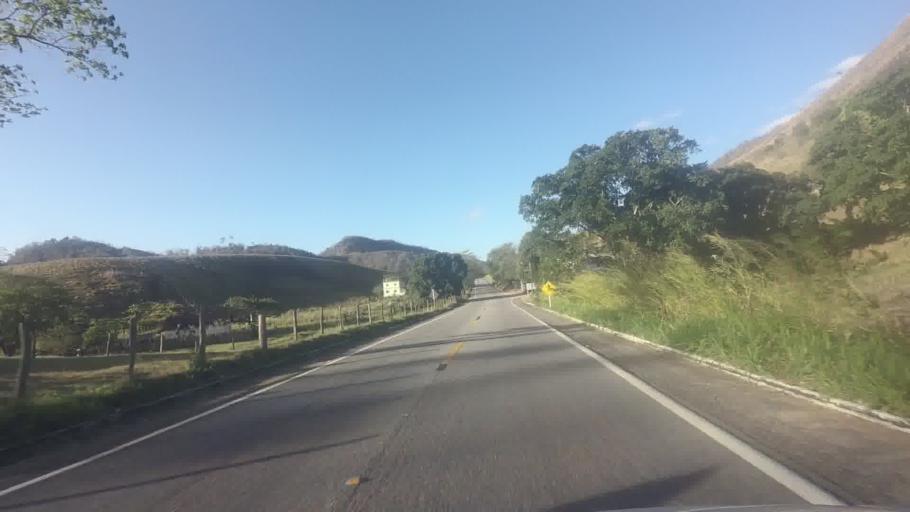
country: BR
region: Espirito Santo
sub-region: Cachoeiro De Itapemirim
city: Cachoeiro de Itapemirim
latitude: -20.8637
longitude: -41.2545
